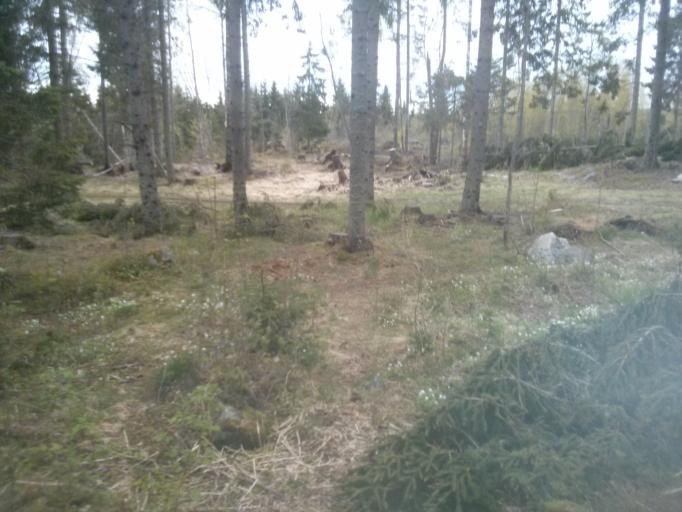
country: SE
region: Vaesternorrland
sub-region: Sundsvalls Kommun
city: Nolby
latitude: 62.2981
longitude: 17.3545
